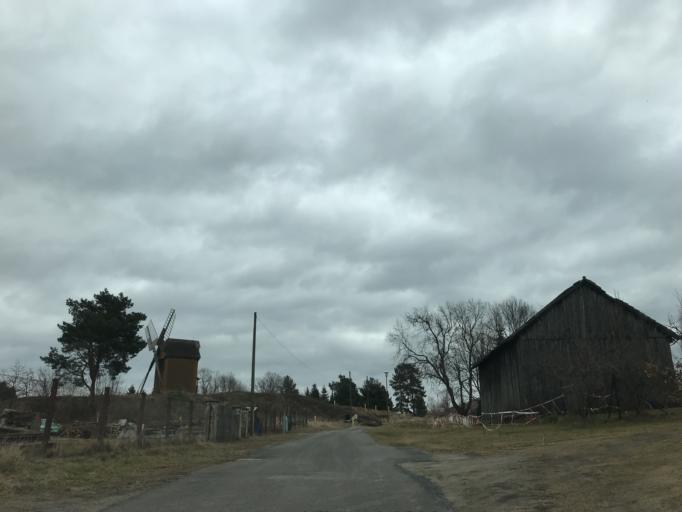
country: DE
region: Brandenburg
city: Crinitz
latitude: 51.7561
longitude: 13.8059
